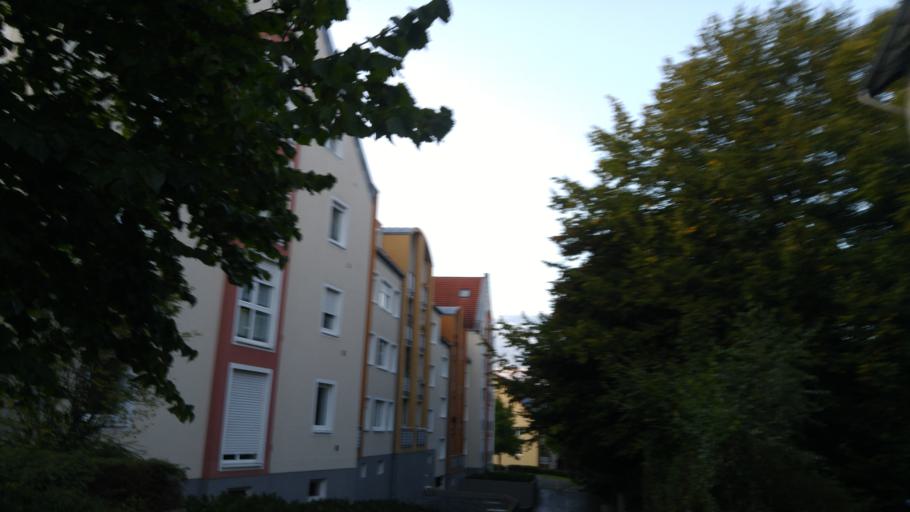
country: DE
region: North Rhine-Westphalia
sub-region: Regierungsbezirk Detmold
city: Bielefeld
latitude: 52.0364
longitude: 8.5257
